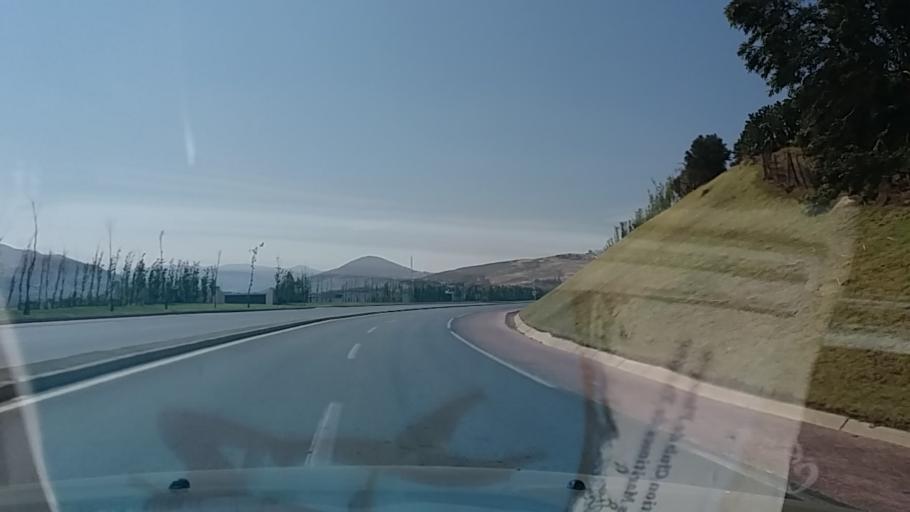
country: MA
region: Tanger-Tetouan
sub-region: Tetouan
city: Saddina
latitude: 35.5598
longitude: -5.4358
